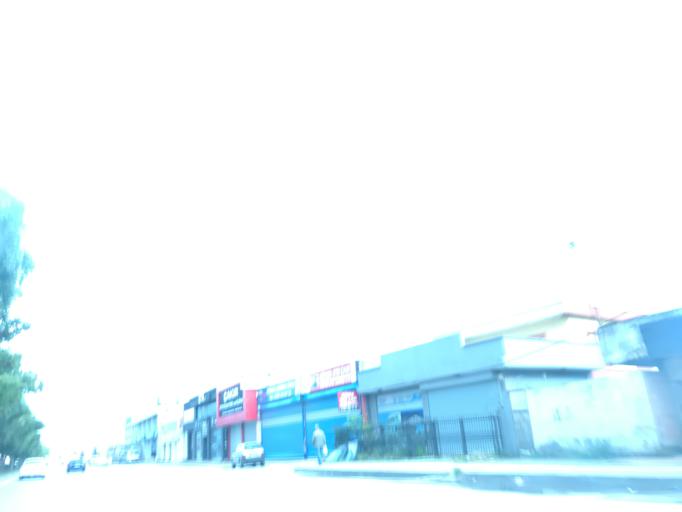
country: TR
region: Adana
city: Seyhan
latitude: 36.9958
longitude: 35.2649
